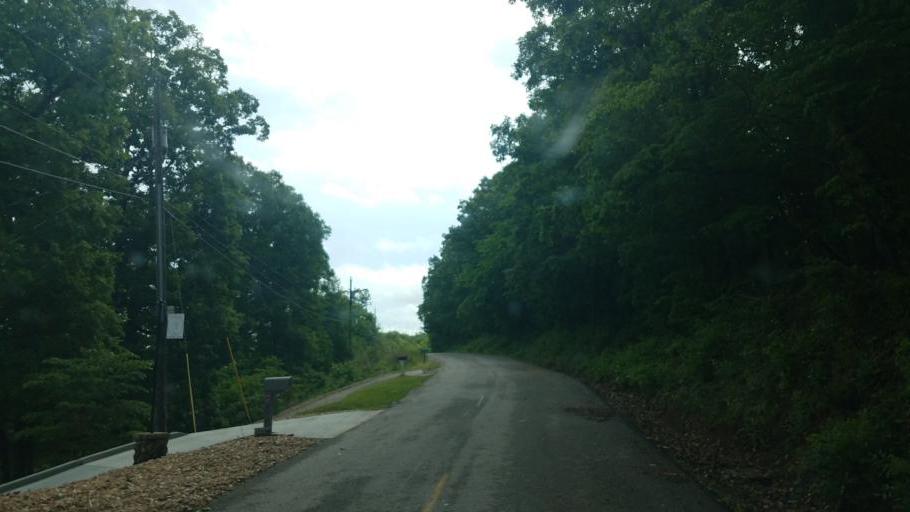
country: US
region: Missouri
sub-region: Camden County
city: Four Seasons
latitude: 38.1708
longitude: -92.6840
